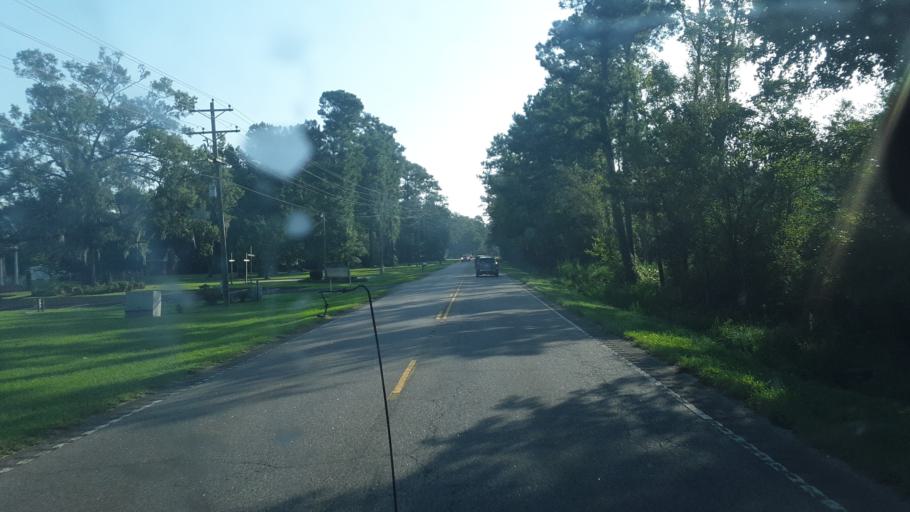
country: US
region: South Carolina
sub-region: Horry County
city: Forestbrook
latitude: 33.8335
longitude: -78.8850
